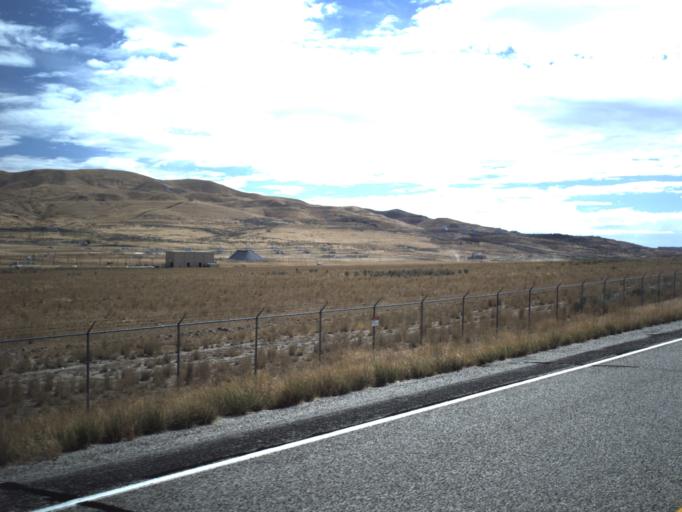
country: US
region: Utah
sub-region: Box Elder County
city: Tremonton
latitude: 41.7135
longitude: -112.4526
